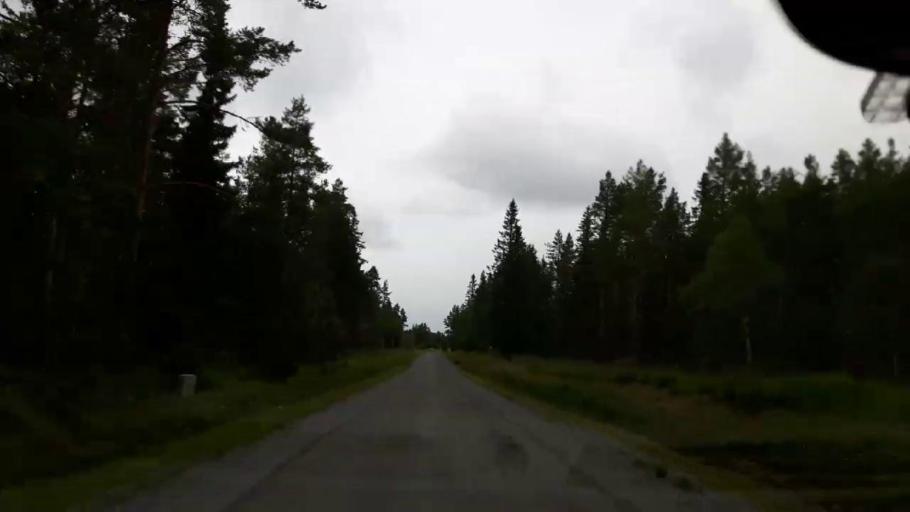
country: SE
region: Jaemtland
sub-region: OEstersunds Kommun
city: Ostersund
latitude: 63.0839
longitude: 14.5551
